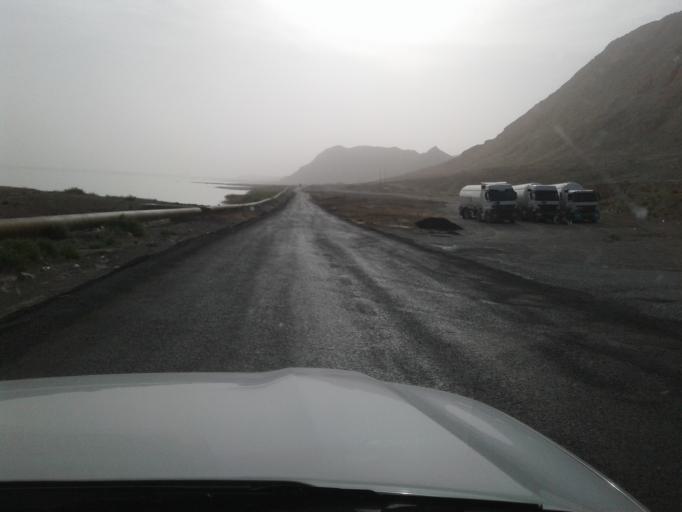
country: TM
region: Balkan
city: Turkmenbasy
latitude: 40.0323
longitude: 52.9305
